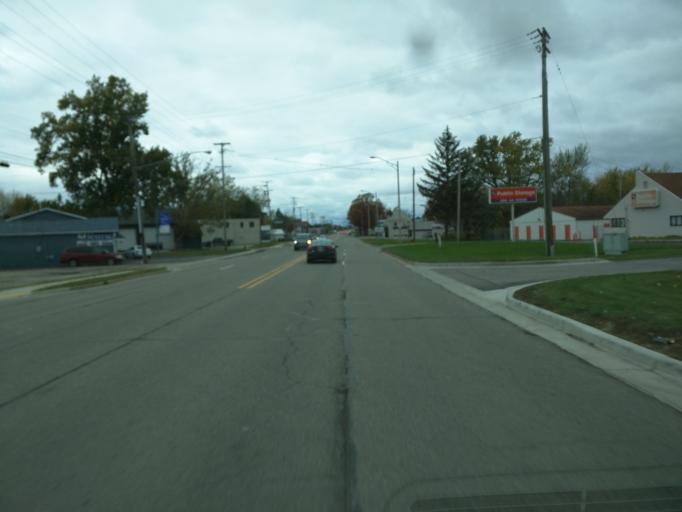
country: US
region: Michigan
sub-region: Ingham County
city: Edgemont Park
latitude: 42.7677
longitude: -84.5942
